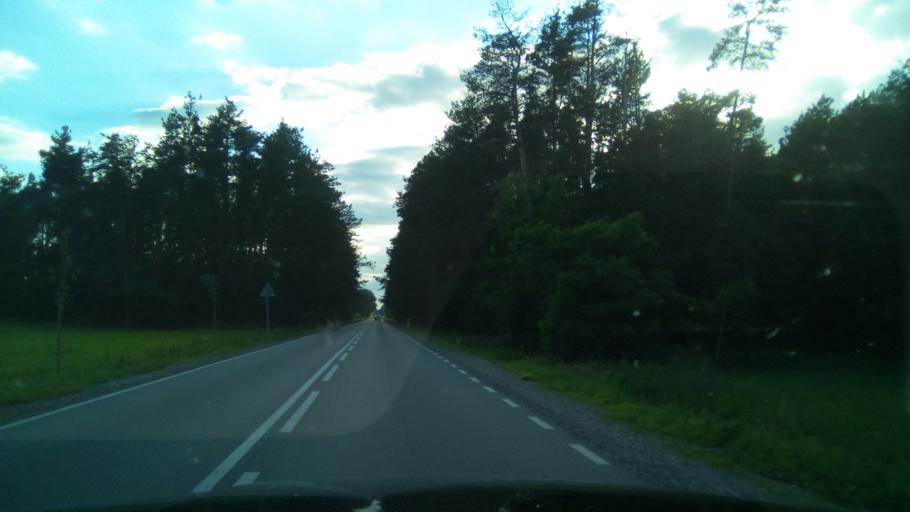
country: PL
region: Masovian Voivodeship
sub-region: Powiat bialobrzeski
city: Promna
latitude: 51.6539
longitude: 21.0069
